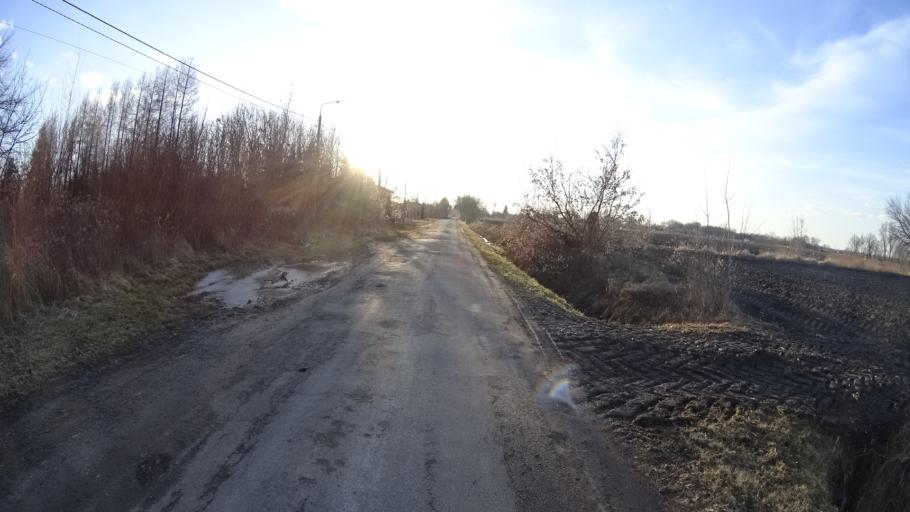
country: PL
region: Masovian Voivodeship
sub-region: Powiat warszawski zachodni
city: Truskaw
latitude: 52.2522
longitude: 20.7461
